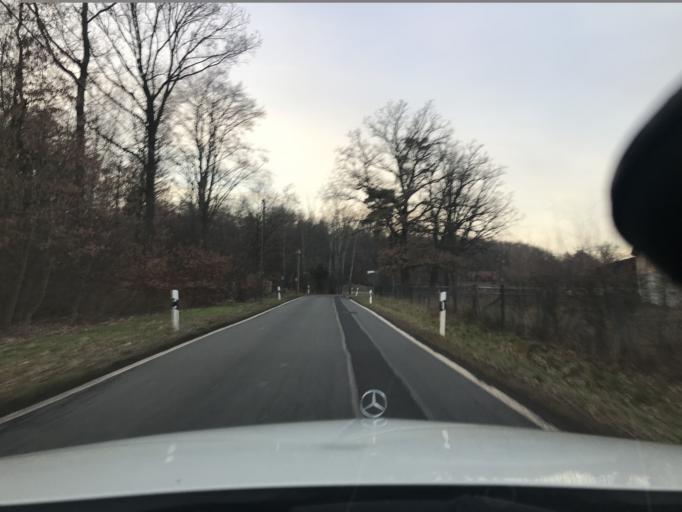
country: DE
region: Thuringia
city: Emleben
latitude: 50.9014
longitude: 10.6580
